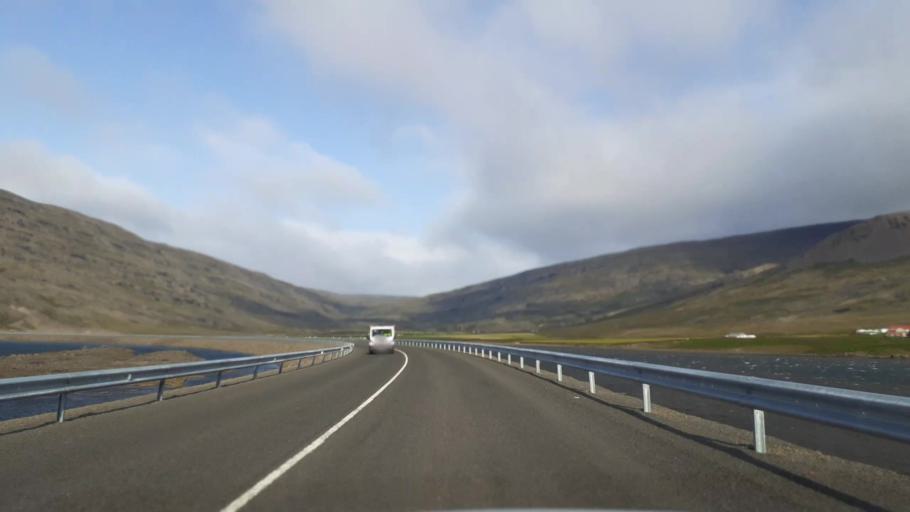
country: IS
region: East
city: Reydarfjoerdur
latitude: 64.7898
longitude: -14.4758
